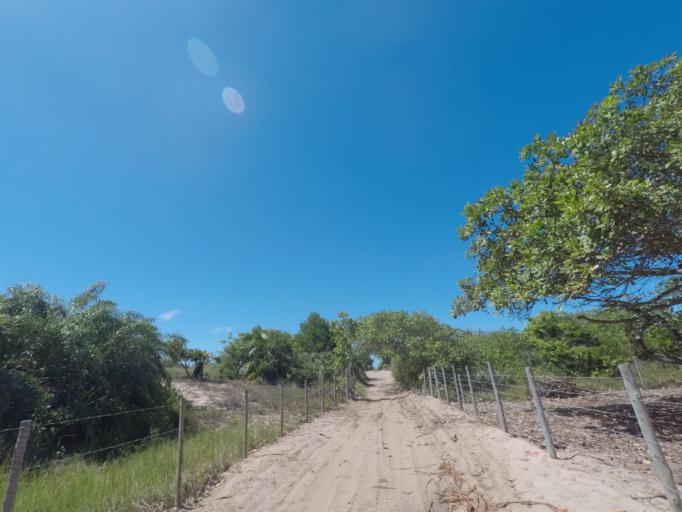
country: BR
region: Bahia
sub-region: Marau
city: Marau
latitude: -13.9582
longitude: -38.9341
